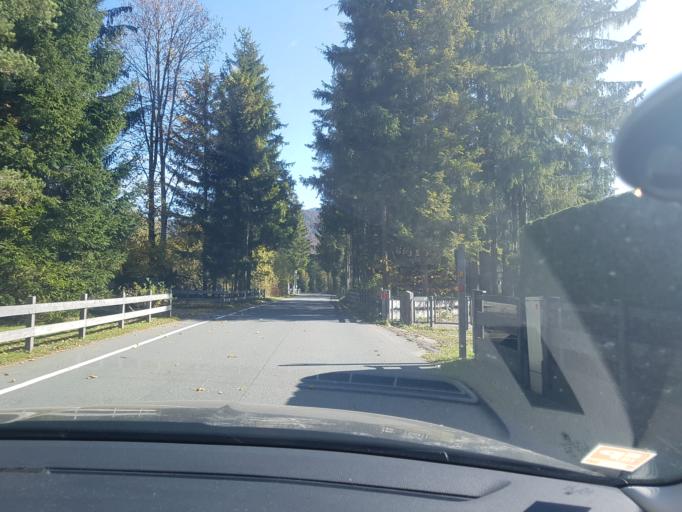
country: AT
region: Tyrol
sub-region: Politischer Bezirk Kitzbuhel
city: Fieberbrunn
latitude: 47.5205
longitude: 12.5816
